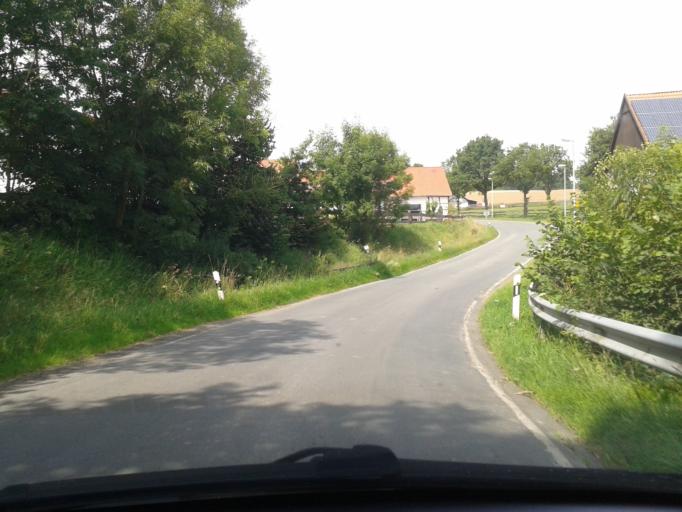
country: DE
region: North Rhine-Westphalia
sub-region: Regierungsbezirk Detmold
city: Lugde
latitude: 51.9599
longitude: 9.1840
